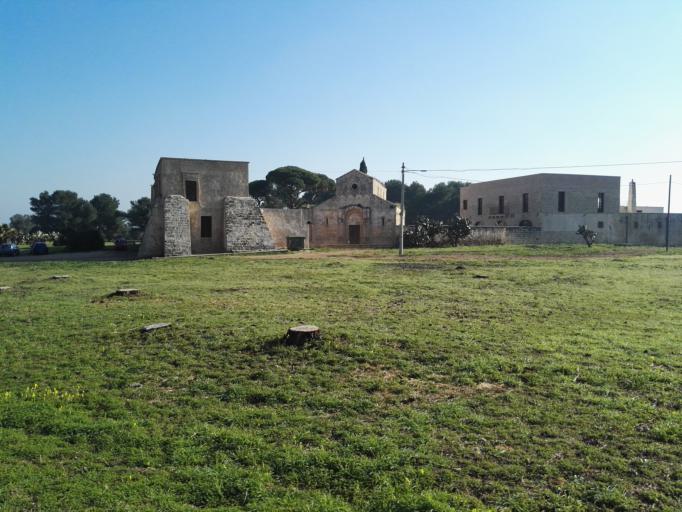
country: IT
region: Apulia
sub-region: Provincia di Lecce
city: Trepuzzi
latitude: 40.4584
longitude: 18.1145
